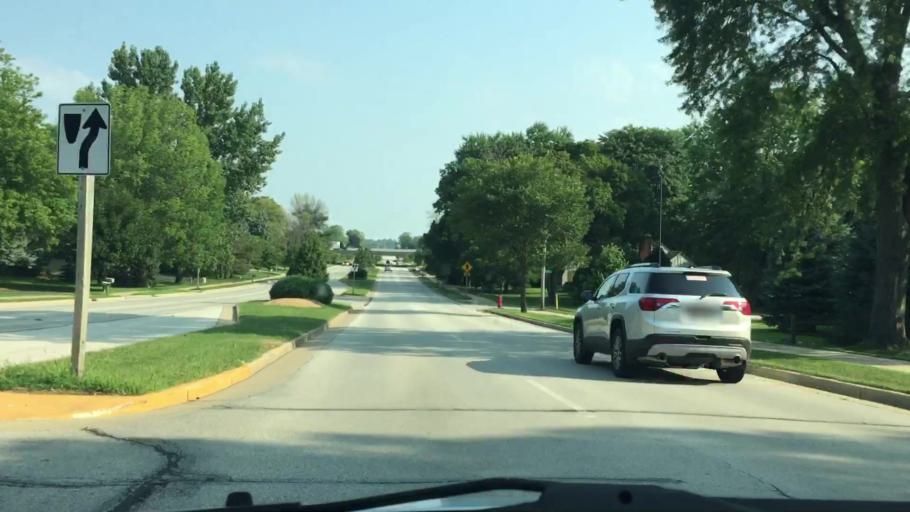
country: US
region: Wisconsin
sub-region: Waukesha County
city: Brookfield
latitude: 43.0244
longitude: -88.1269
